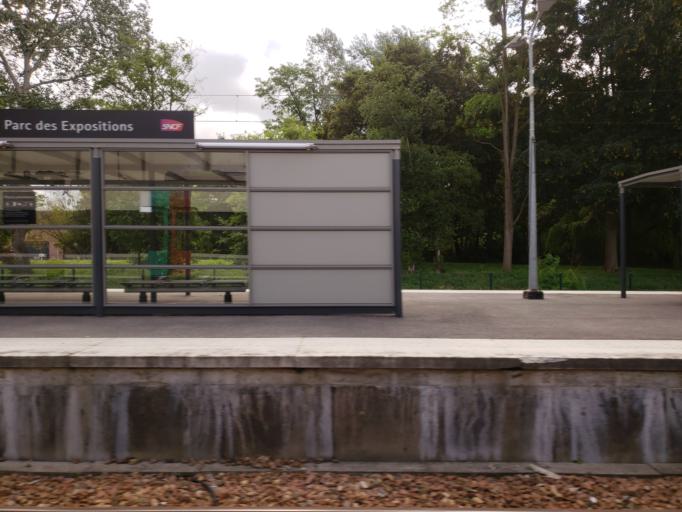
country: FR
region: Ile-de-France
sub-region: Departement de Seine-Saint-Denis
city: Villepinte
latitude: 48.9742
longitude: 2.5149
